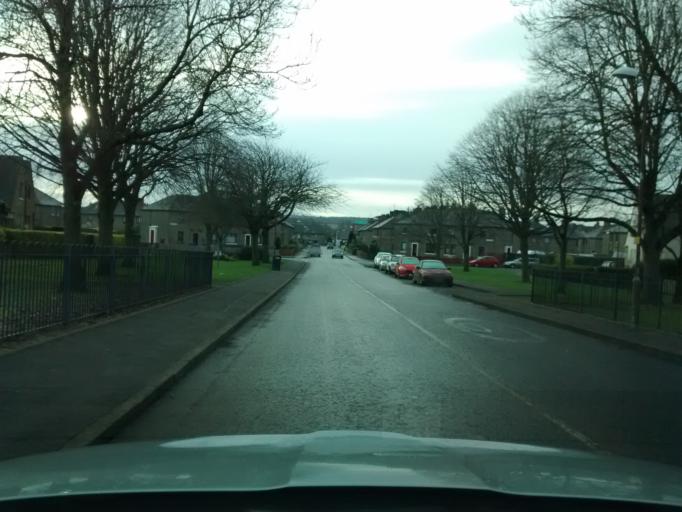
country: GB
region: Scotland
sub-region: West Lothian
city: Broxburn
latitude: 55.9347
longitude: -3.4886
